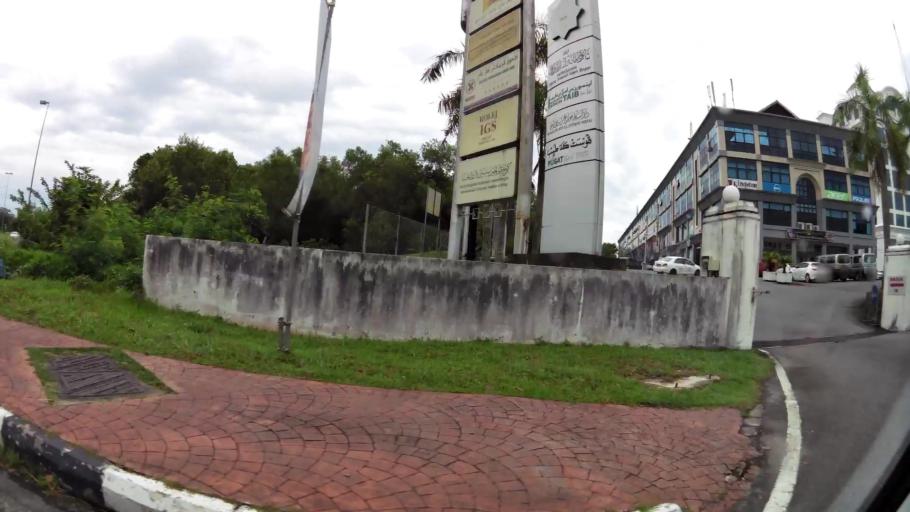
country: BN
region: Brunei and Muara
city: Bandar Seri Begawan
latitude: 4.9005
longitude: 114.9256
